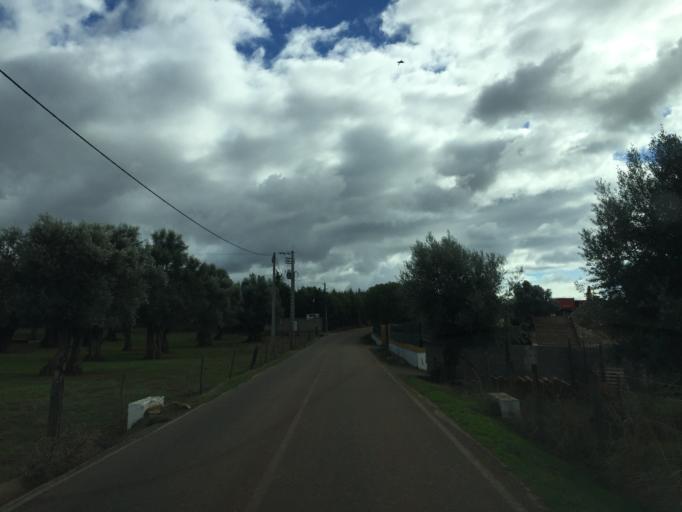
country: PT
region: Portalegre
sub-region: Alter do Chao
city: Alter do Chao
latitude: 39.2096
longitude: -7.6662
